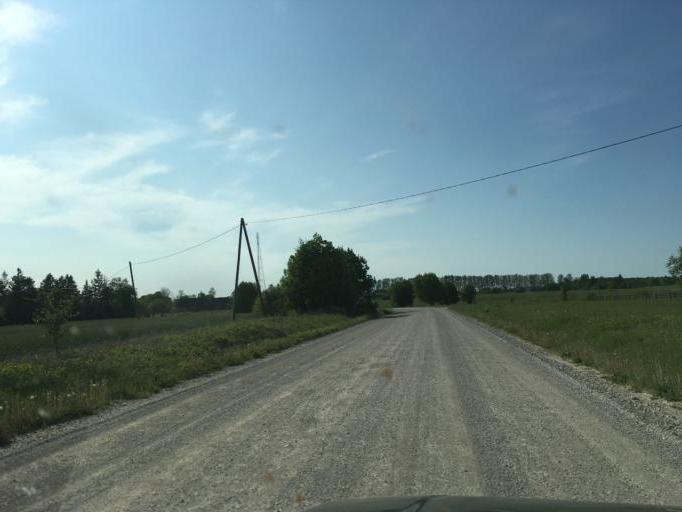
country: LV
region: Dundaga
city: Dundaga
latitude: 57.6081
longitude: 22.4601
